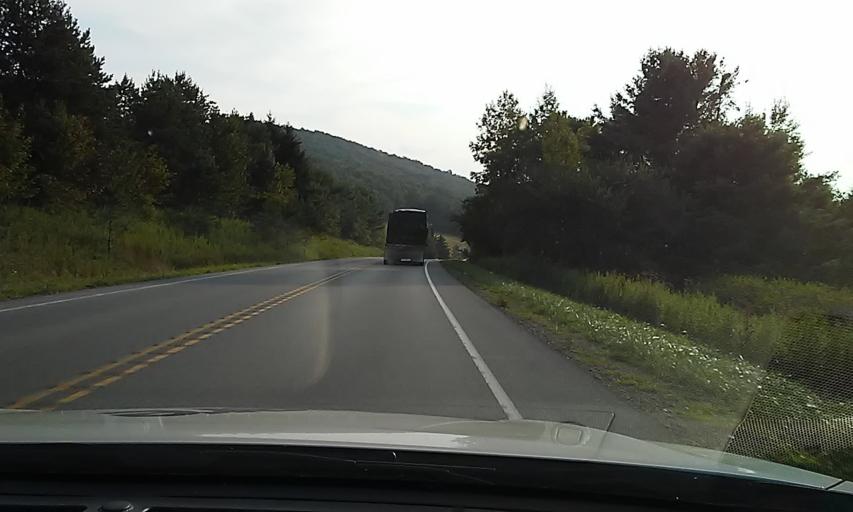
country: US
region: Pennsylvania
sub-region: McKean County
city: Smethport
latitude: 41.7094
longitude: -78.5679
